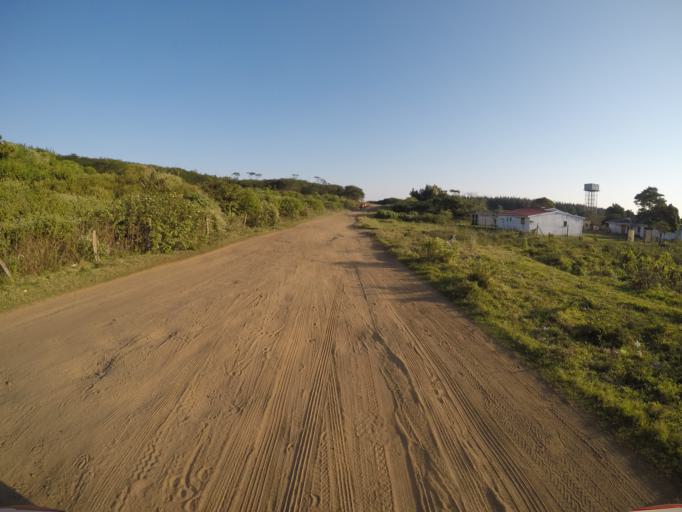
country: ZA
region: KwaZulu-Natal
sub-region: uThungulu District Municipality
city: KwaMbonambi
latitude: -28.7071
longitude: 32.1852
